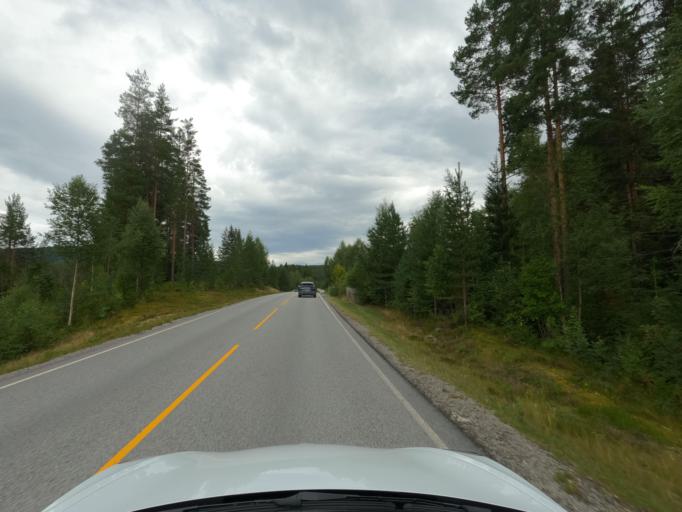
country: NO
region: Telemark
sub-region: Hjartdal
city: Sauland
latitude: 59.7044
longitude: 9.0123
